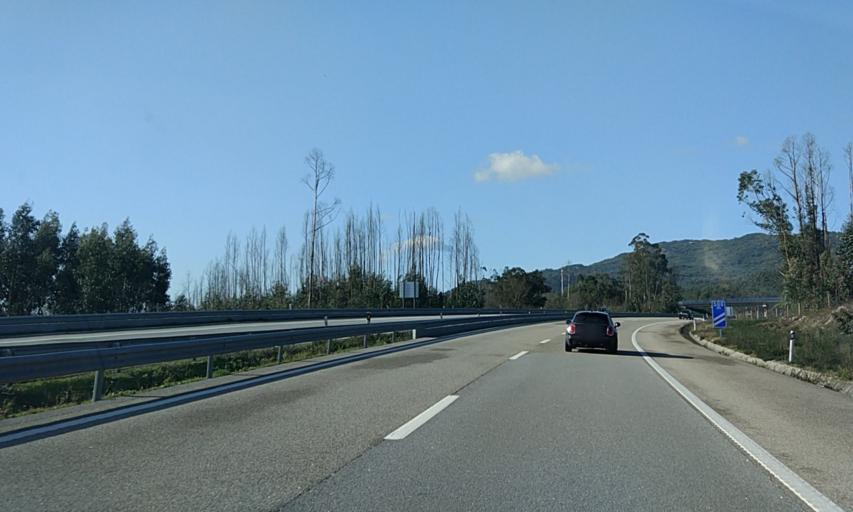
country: PT
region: Viseu
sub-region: Oliveira de Frades
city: Oliveira de Frades
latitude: 40.6846
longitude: -8.2580
